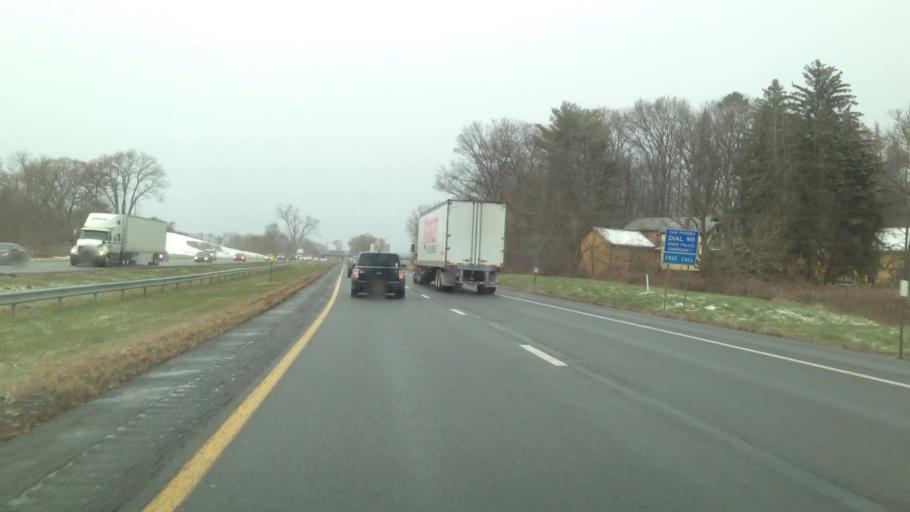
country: US
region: New York
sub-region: Rensselaer County
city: Castleton-on-Hudson
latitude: 42.5546
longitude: -73.7839
